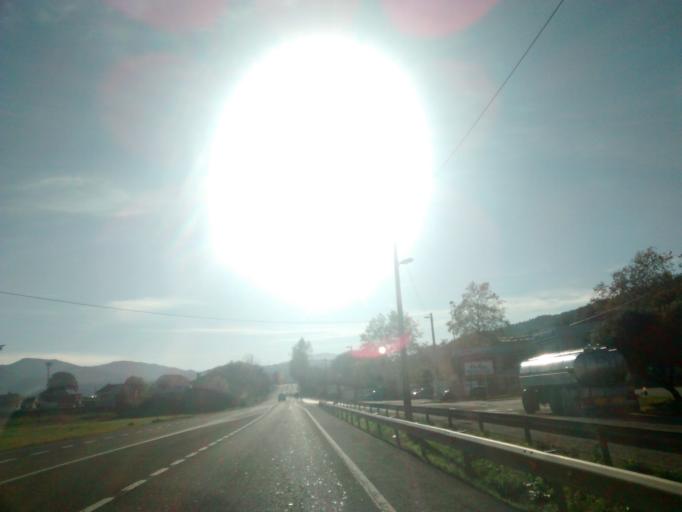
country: ES
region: Cantabria
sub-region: Provincia de Cantabria
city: Puente Viesgo
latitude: 43.3282
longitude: -3.9673
